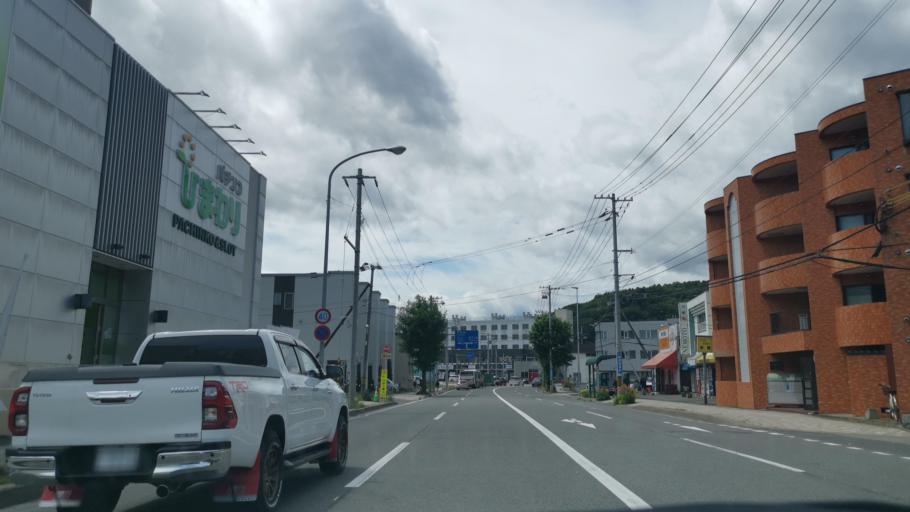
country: JP
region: Hokkaido
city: Sapporo
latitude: 43.0058
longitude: 141.3500
